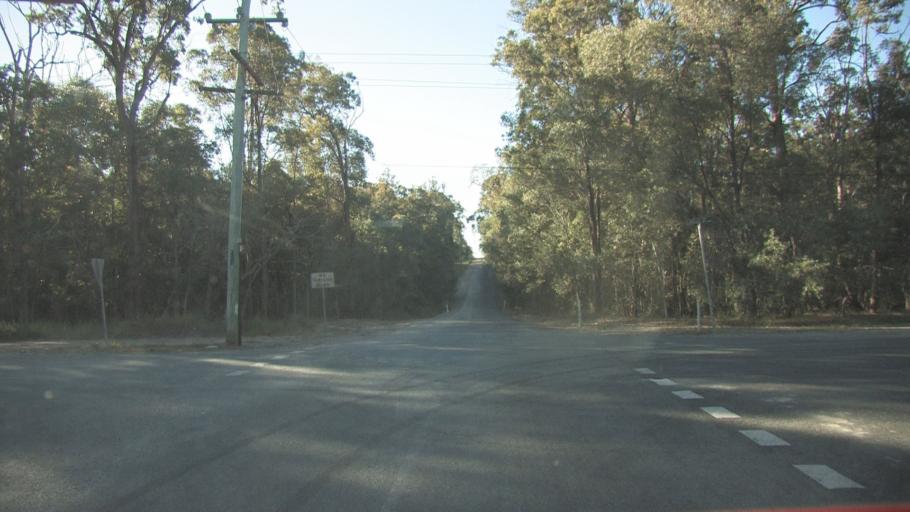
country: AU
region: Queensland
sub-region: Logan
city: Chambers Flat
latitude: -27.7613
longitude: 153.1233
